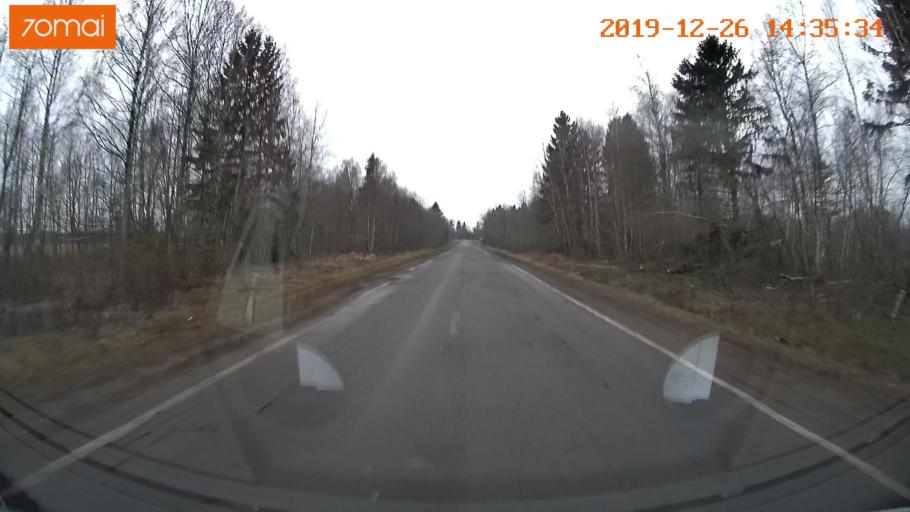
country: RU
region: Jaroslavl
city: Poshekhon'ye
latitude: 58.4192
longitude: 38.9829
